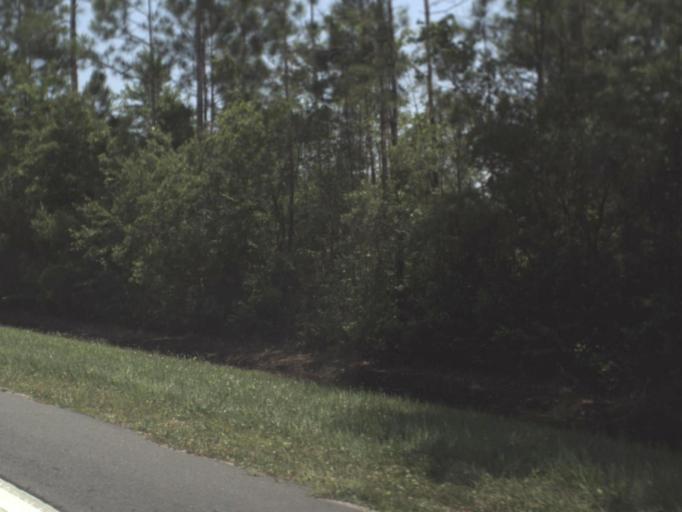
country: US
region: Florida
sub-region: Duval County
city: Baldwin
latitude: 30.2045
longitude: -81.9891
